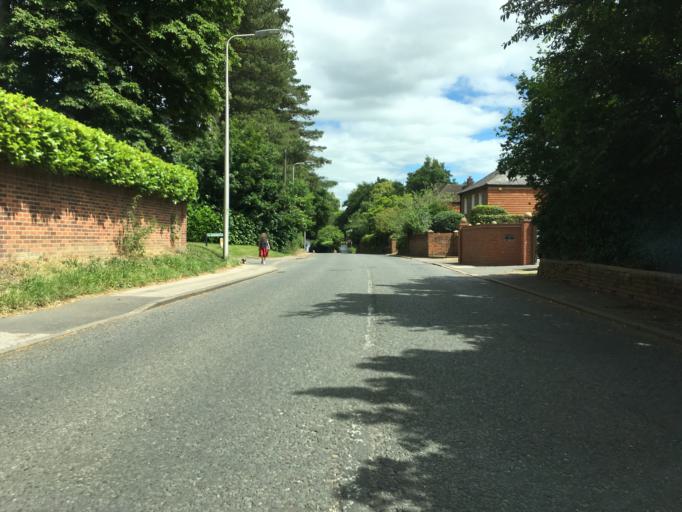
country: GB
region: England
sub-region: West Berkshire
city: Newbury
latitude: 51.3841
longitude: -1.3377
